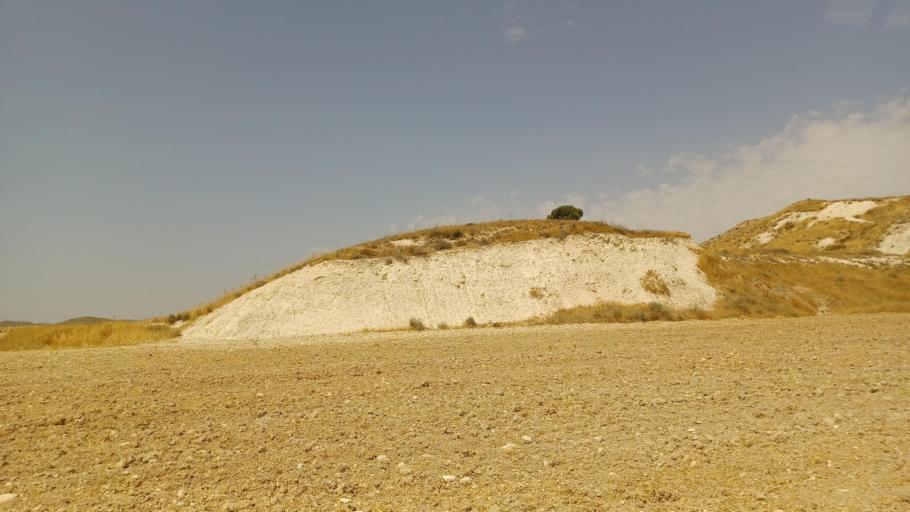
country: CY
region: Larnaka
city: Troulloi
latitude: 35.0325
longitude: 33.5931
